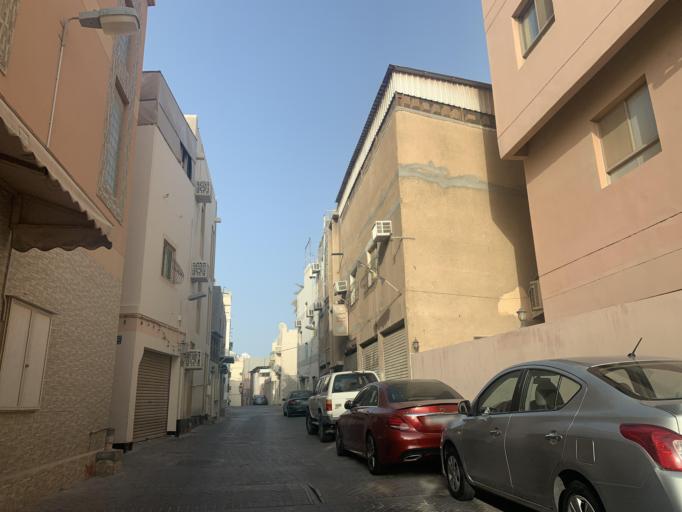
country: BH
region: Manama
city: Jidd Hafs
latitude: 26.2233
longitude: 50.5472
